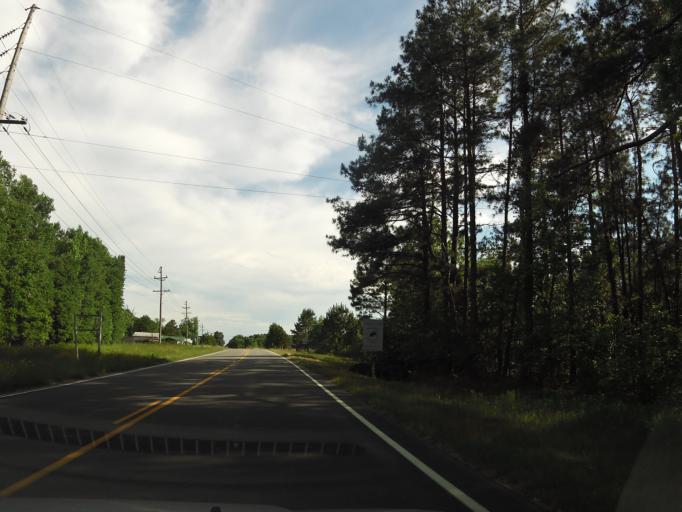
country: US
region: South Carolina
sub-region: Allendale County
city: Fairfax
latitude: 32.9435
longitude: -81.2368
